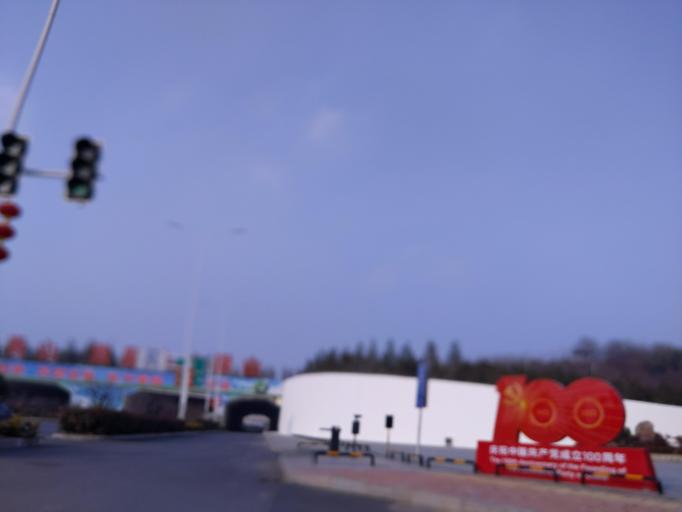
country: CN
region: Henan Sheng
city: Puyang
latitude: 35.8174
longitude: 115.0227
